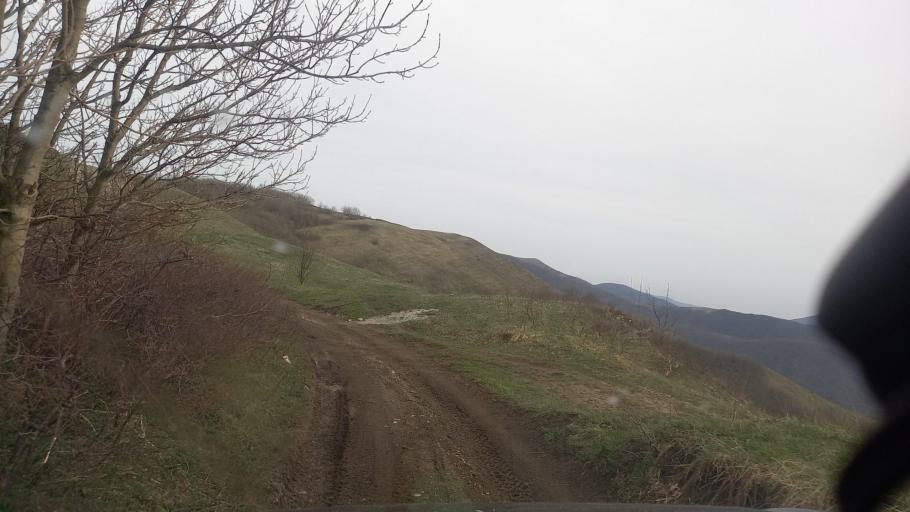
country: RU
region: Krasnodarskiy
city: Gelendzhik
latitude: 44.6147
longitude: 38.1994
